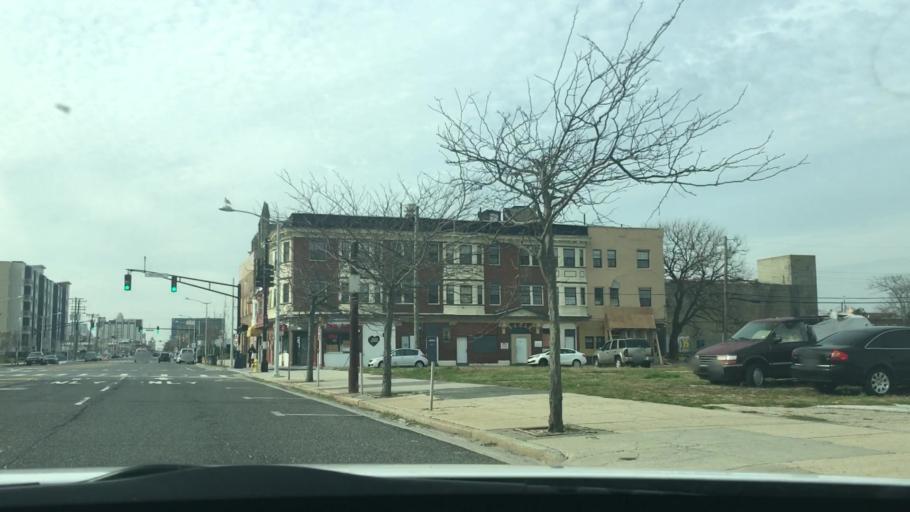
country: US
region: New Jersey
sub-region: Atlantic County
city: Atlantic City
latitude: 39.3670
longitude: -74.4163
